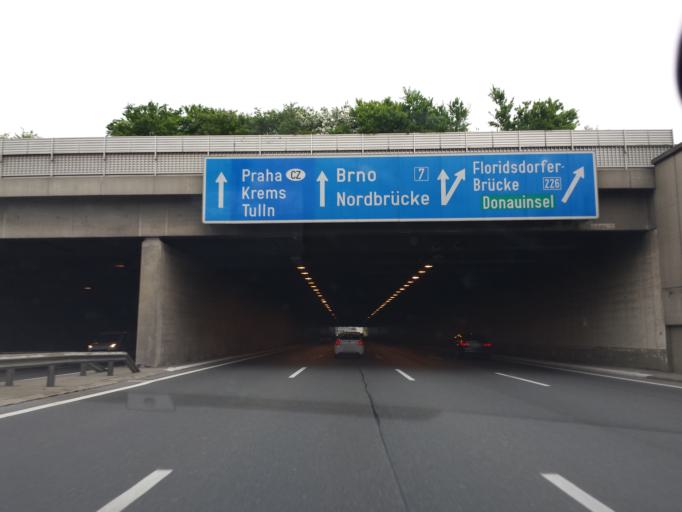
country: AT
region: Vienna
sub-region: Wien Stadt
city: Vienna
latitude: 48.2443
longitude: 16.3977
